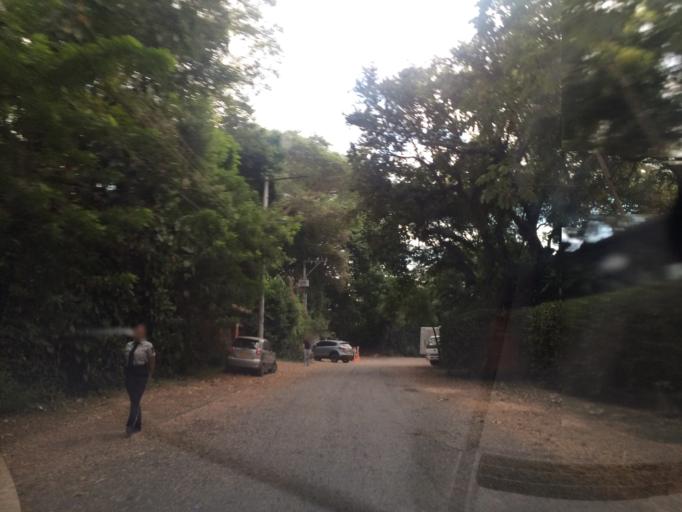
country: CO
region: Valle del Cauca
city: Cali
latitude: 3.3957
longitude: -76.5551
